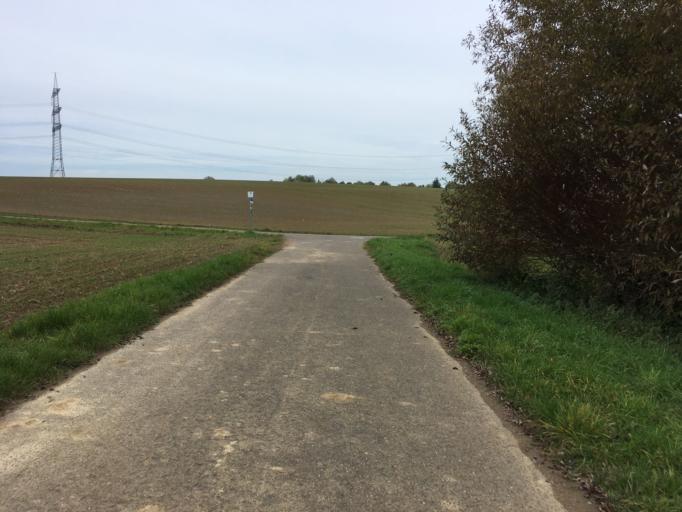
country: DE
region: Baden-Wuerttemberg
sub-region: Karlsruhe Region
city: Seckach
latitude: 49.4568
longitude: 9.3285
